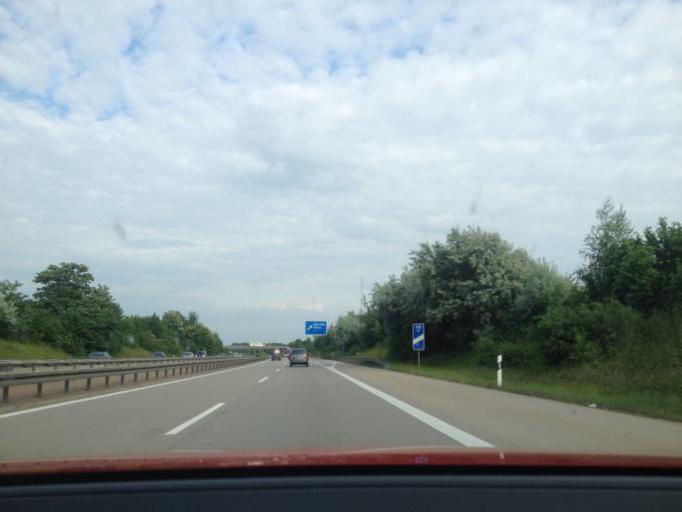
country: DE
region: Saxony-Anhalt
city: Trebitz
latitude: 51.5754
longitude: 11.8966
